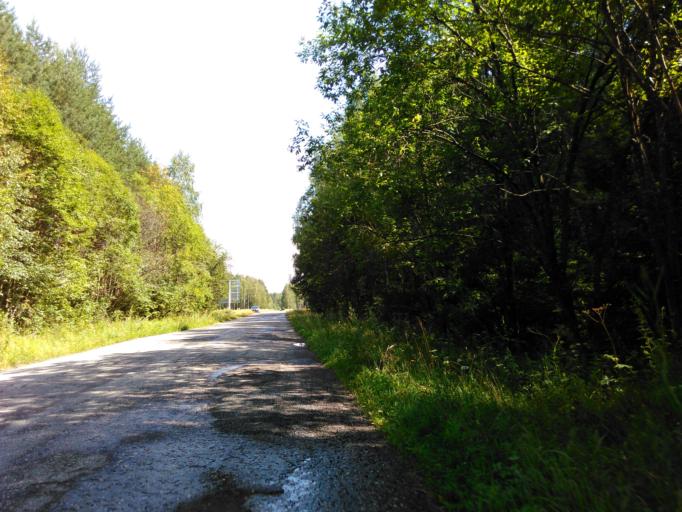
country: RU
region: Moskovskaya
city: Elektrogorsk
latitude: 56.0243
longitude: 38.7777
